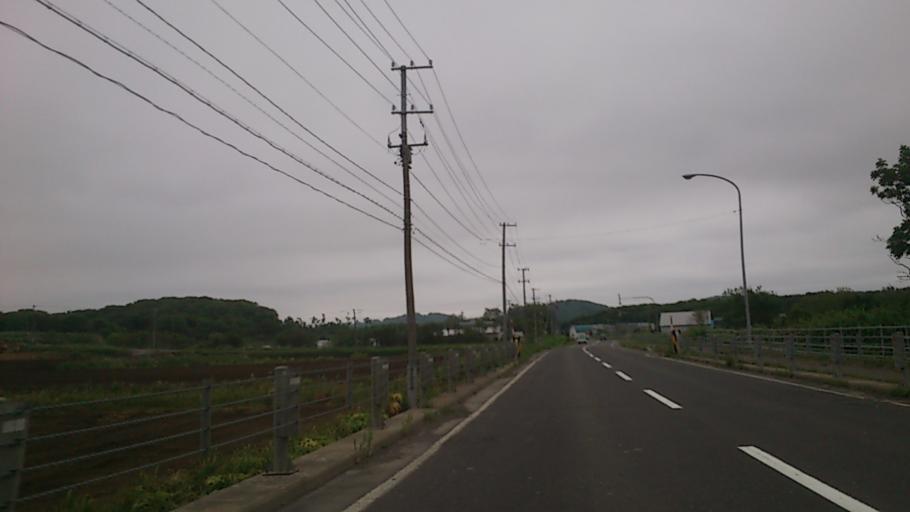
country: JP
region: Hokkaido
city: Iwanai
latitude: 42.4243
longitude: 139.8578
